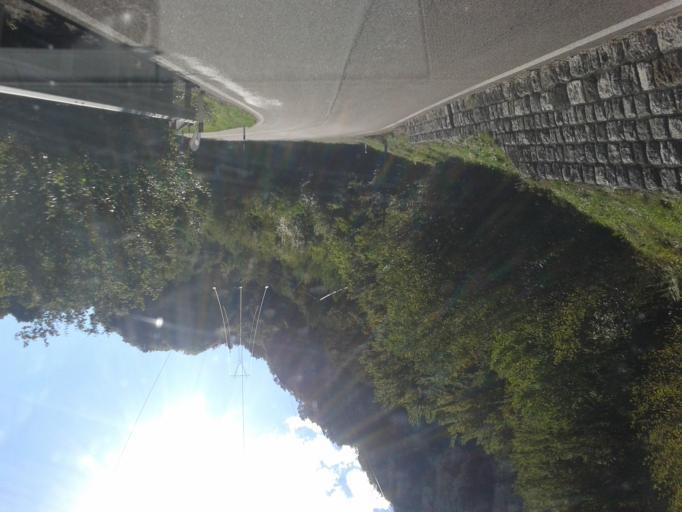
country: IT
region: Trentino-Alto Adige
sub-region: Provincia di Trento
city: Molina di Ledro
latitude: 45.8783
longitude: 10.7675
